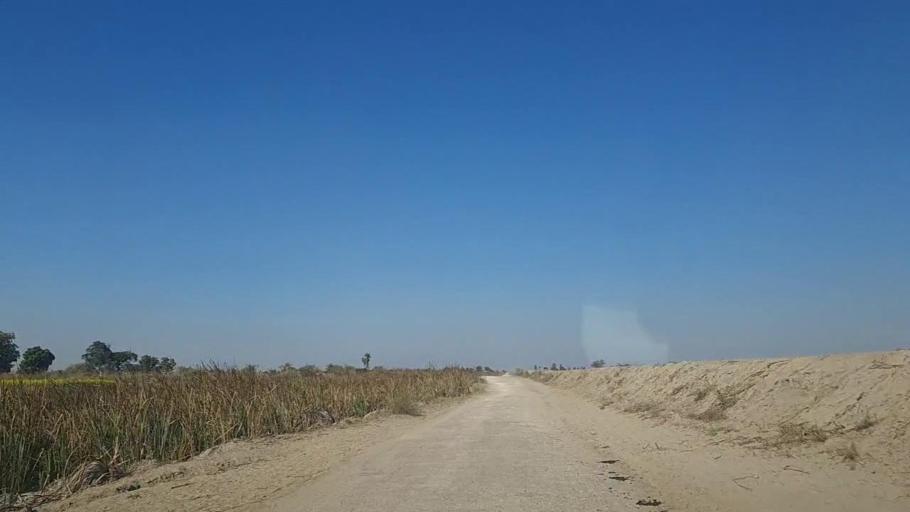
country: PK
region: Sindh
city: Sanghar
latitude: 26.2126
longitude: 68.9293
